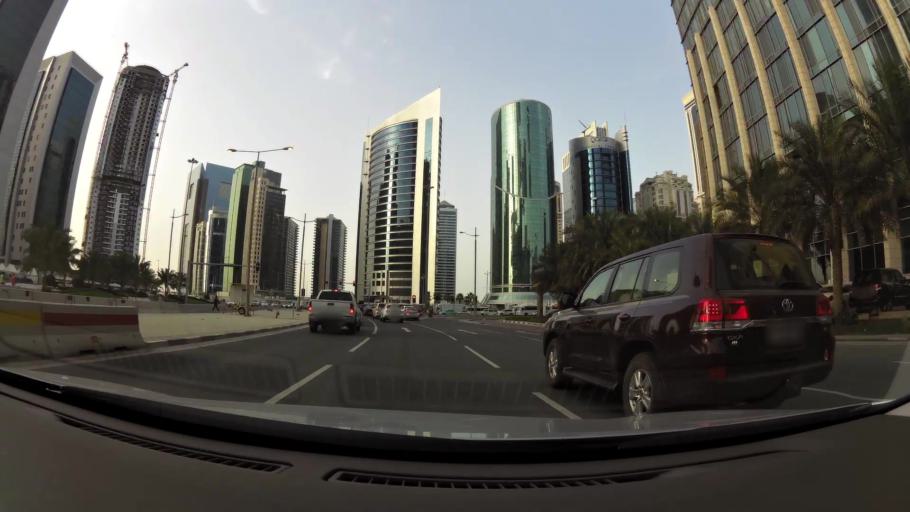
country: QA
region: Baladiyat ad Dawhah
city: Doha
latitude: 25.3251
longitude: 51.5277
